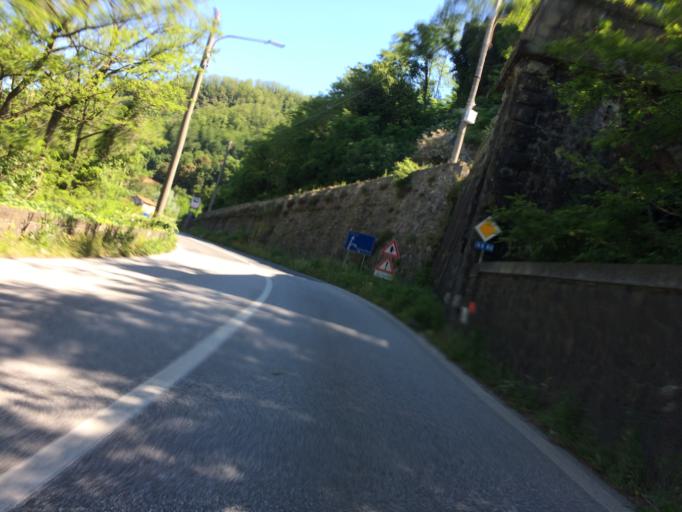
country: IT
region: Tuscany
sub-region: Provincia di Massa-Carrara
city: Albiano Magra
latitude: 44.1749
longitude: 9.9283
